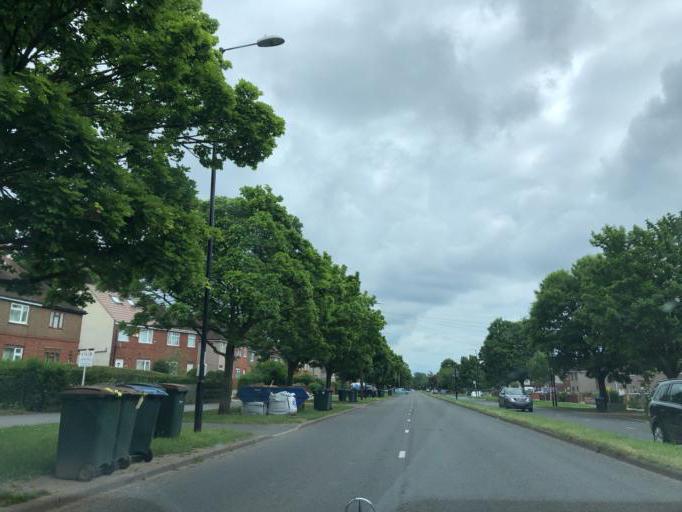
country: GB
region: England
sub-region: Warwickshire
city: Kenilworth
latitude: 52.3922
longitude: -1.5680
